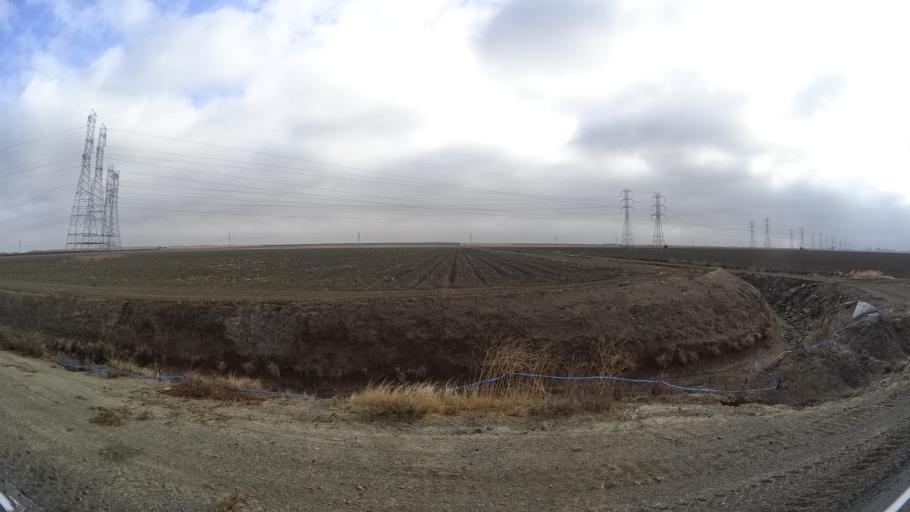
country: US
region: California
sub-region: Yolo County
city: Esparto
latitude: 38.7664
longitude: -122.0071
